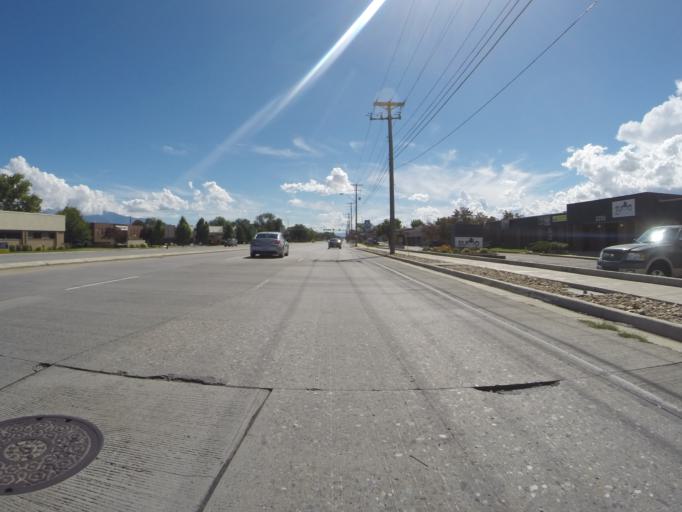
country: US
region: Utah
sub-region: Salt Lake County
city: South Salt Lake
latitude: 40.7225
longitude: -111.9391
